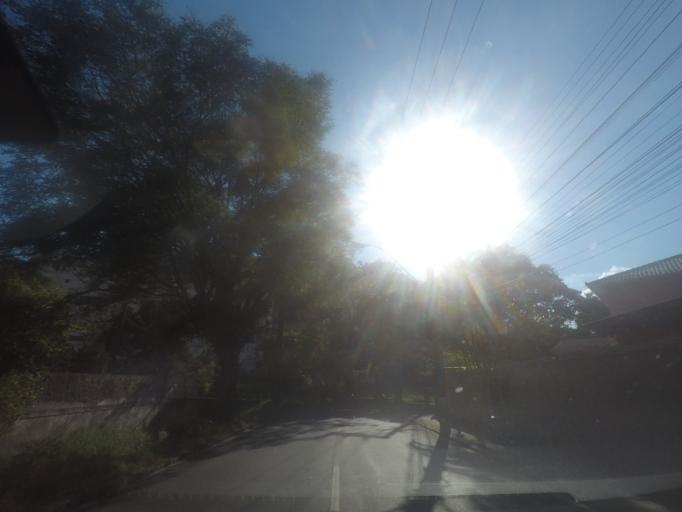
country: BR
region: Rio de Janeiro
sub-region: Petropolis
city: Petropolis
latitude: -22.5153
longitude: -43.1703
